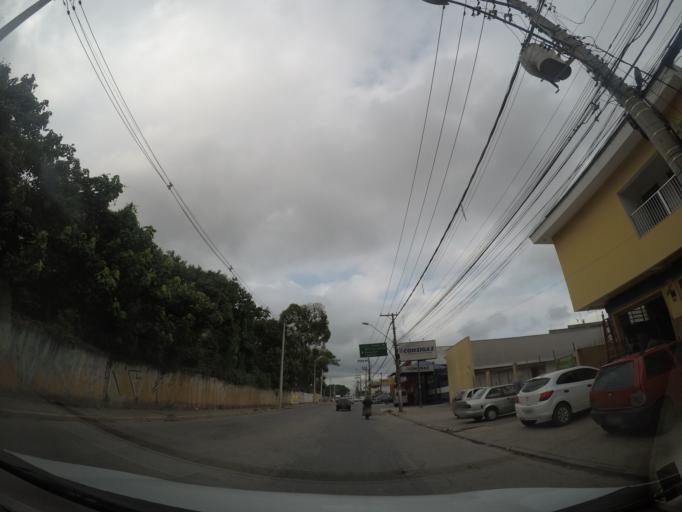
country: BR
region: Sao Paulo
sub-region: Aruja
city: Aruja
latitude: -23.4062
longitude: -46.4076
